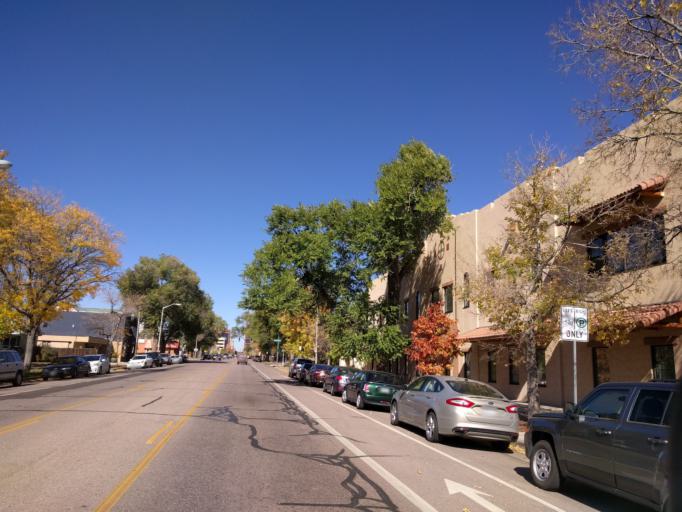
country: US
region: Colorado
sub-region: El Paso County
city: Colorado Springs
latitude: 38.8233
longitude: -104.8241
